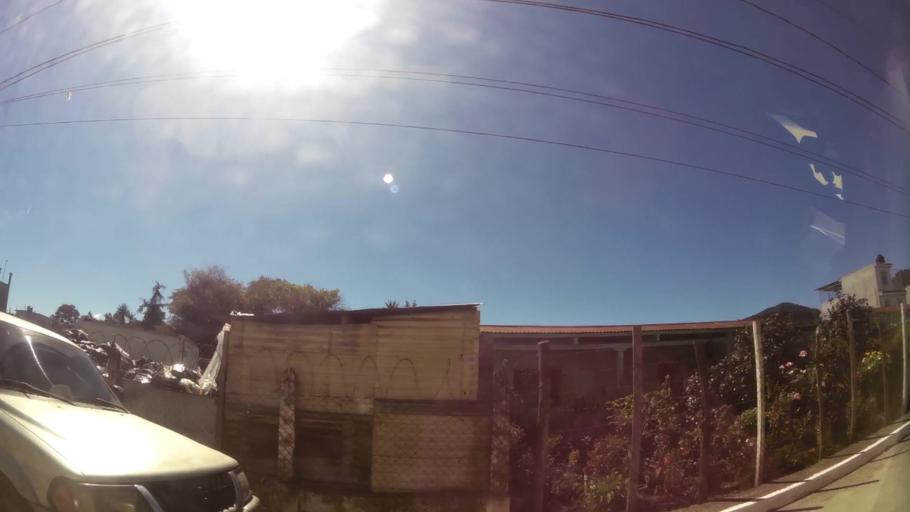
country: GT
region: Guatemala
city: San Jose Pinula
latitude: 14.5404
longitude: -90.4117
